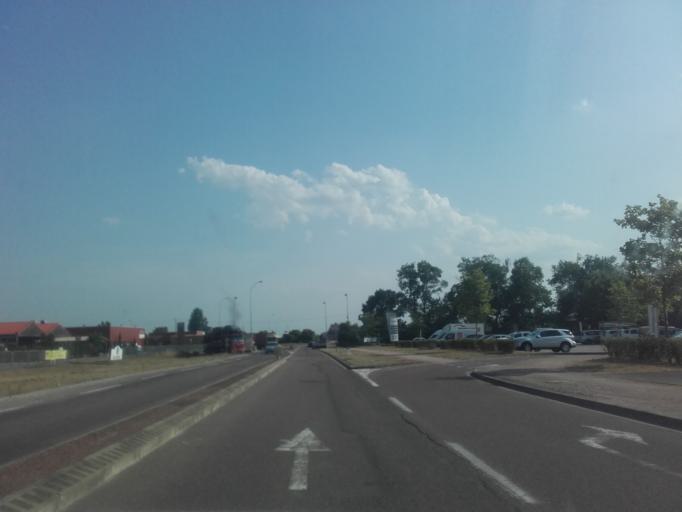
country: FR
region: Bourgogne
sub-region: Departement de la Cote-d'Or
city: Beaune
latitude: 47.0209
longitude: 4.8573
